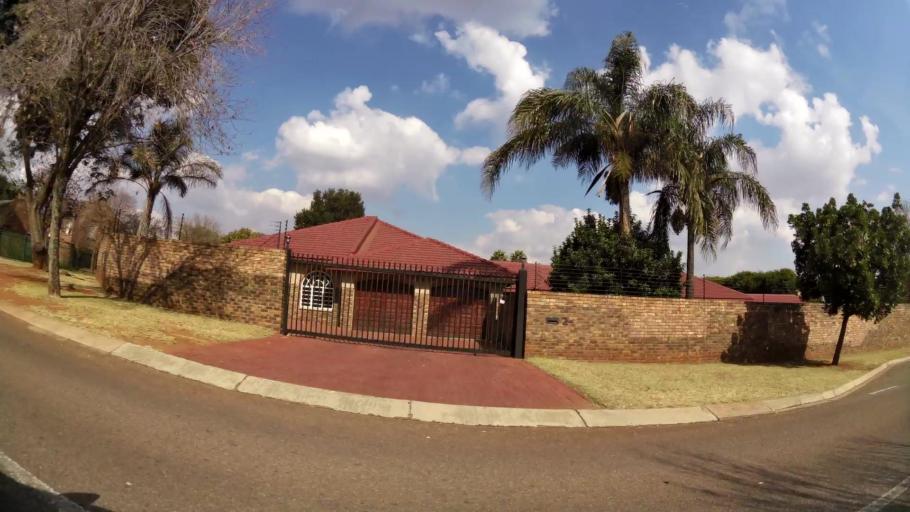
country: ZA
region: Gauteng
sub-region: City of Tshwane Metropolitan Municipality
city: Centurion
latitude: -25.8318
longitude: 28.2355
